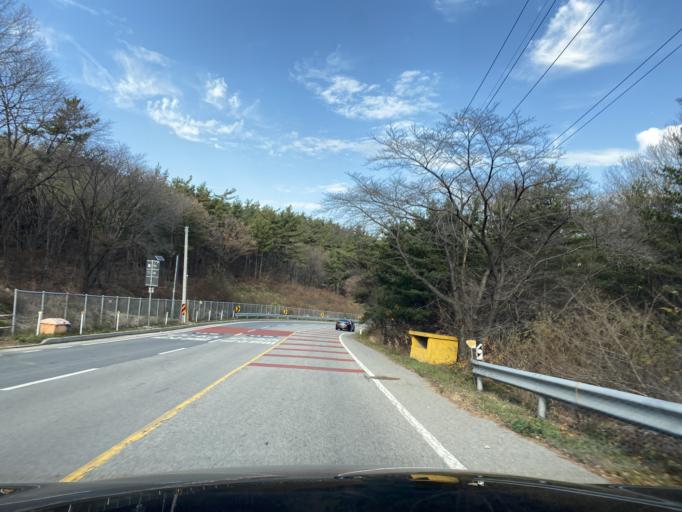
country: KR
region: Chungcheongnam-do
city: Hongsung
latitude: 36.6682
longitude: 126.6382
